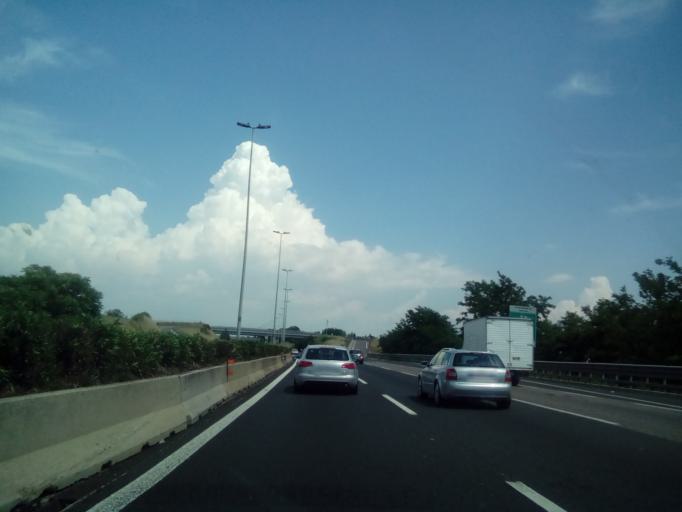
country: IT
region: Latium
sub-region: Citta metropolitana di Roma Capitale
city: Selcetta
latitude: 41.7944
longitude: 12.5071
